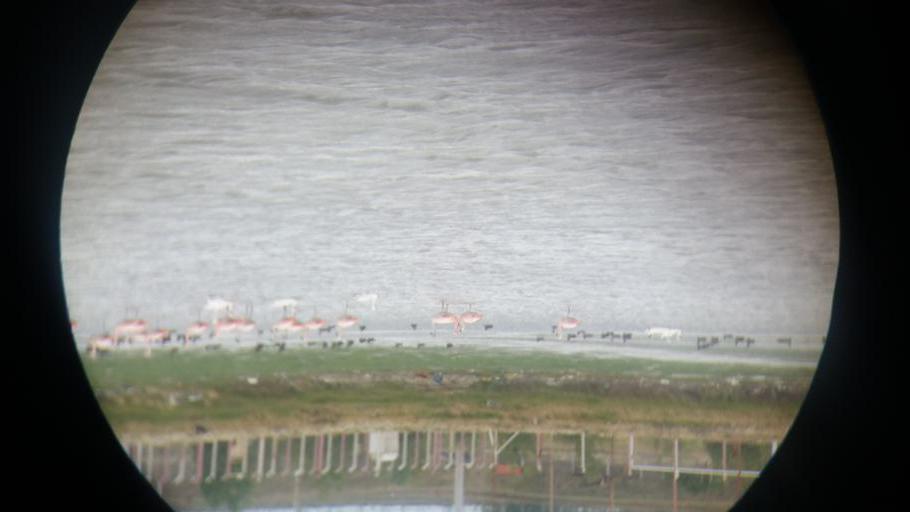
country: AR
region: Santa Cruz
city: Rio Gallegos
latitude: -51.6465
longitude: -69.2411
